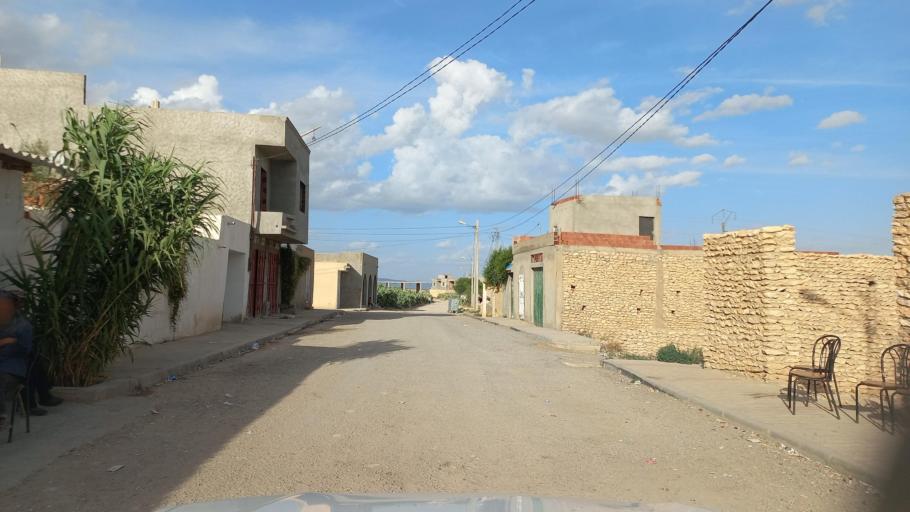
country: TN
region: Al Qasrayn
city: Sbiba
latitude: 35.4456
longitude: 9.0796
